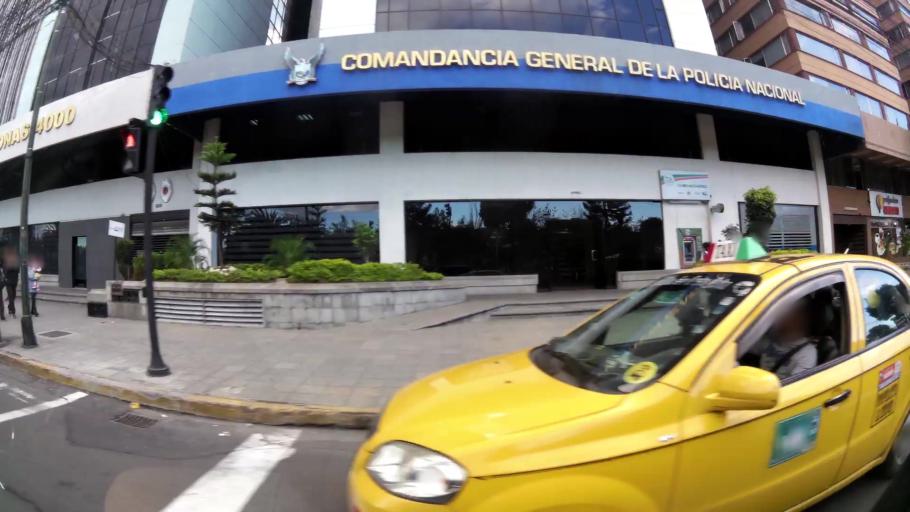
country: EC
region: Pichincha
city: Quito
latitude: -0.1795
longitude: -78.4863
